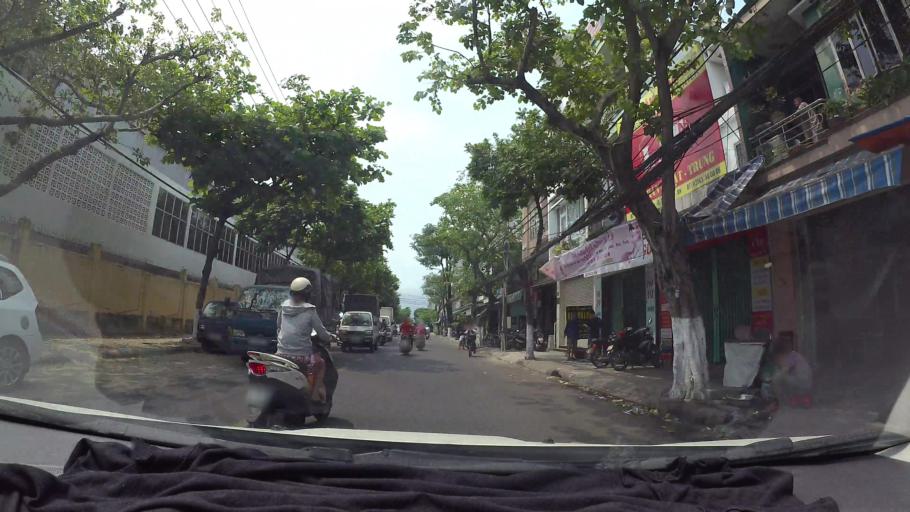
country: VN
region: Da Nang
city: Da Nang
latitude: 16.0721
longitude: 108.2066
